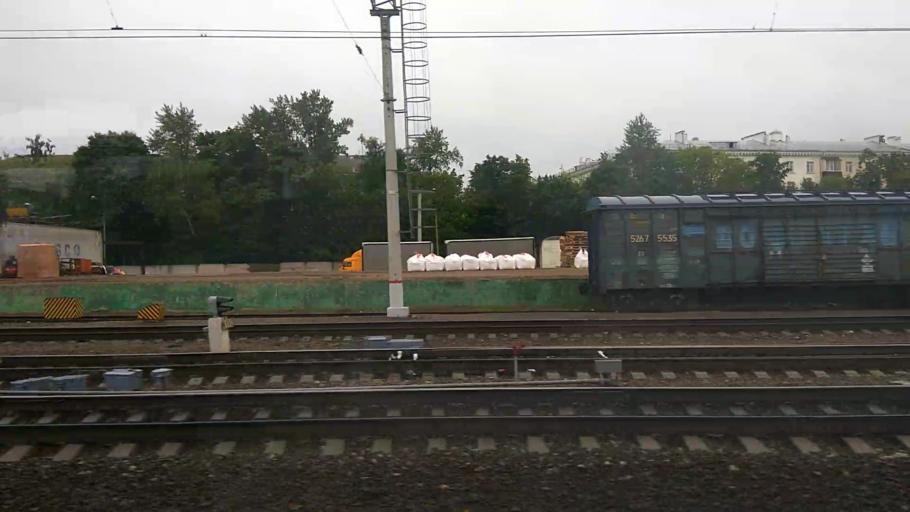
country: RU
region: Moskovskaya
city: Lyubertsy
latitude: 55.6803
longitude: 37.9004
